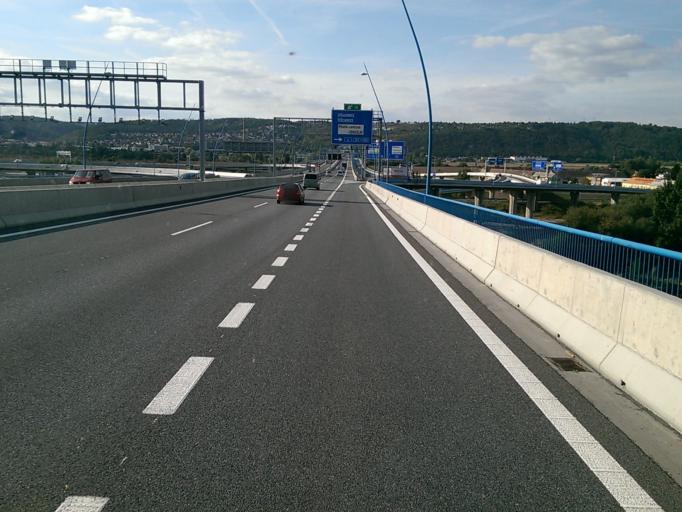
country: CZ
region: Praha
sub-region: Praha 12
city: Modrany
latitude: 49.9839
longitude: 14.4002
